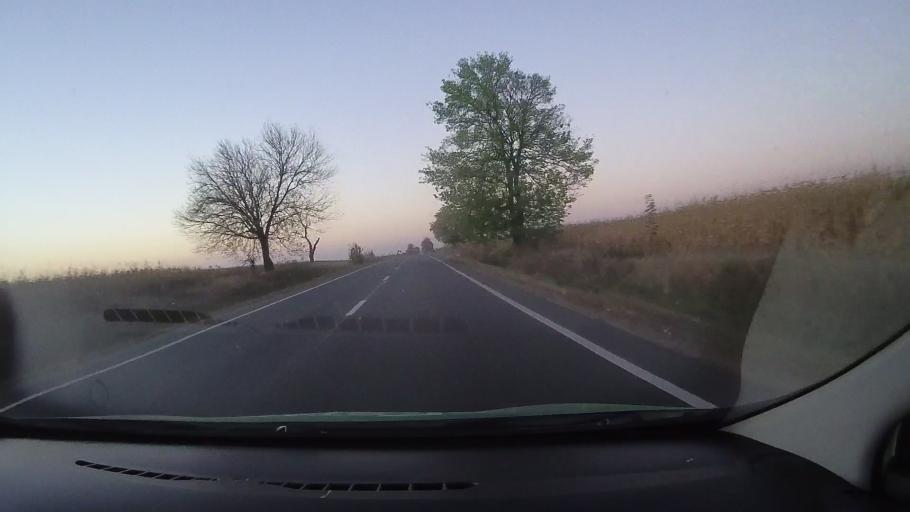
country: RO
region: Bihor
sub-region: Comuna Tarcea
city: Tarcea
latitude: 47.4722
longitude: 22.1649
